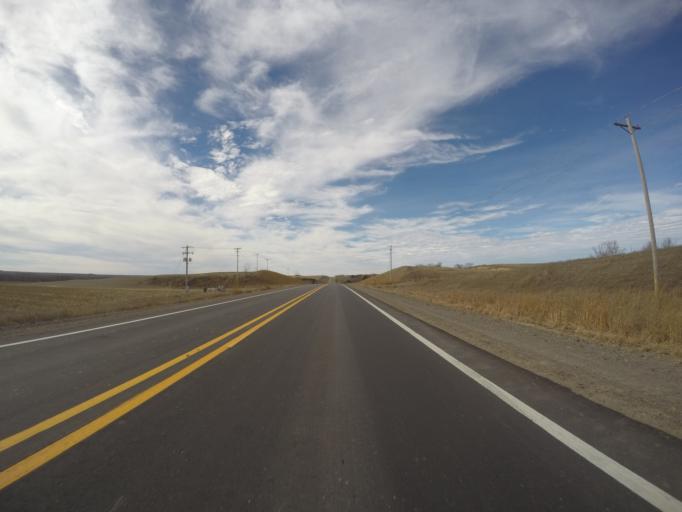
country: US
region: Nebraska
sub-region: Franklin County
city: Franklin
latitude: 40.0962
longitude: -98.8665
